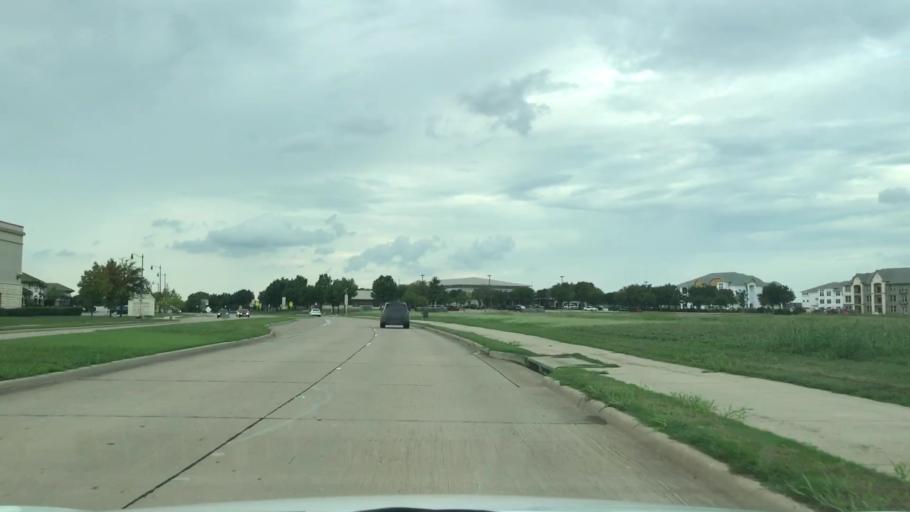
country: US
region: Texas
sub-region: Collin County
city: Frisco
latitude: 33.1289
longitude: -96.8071
